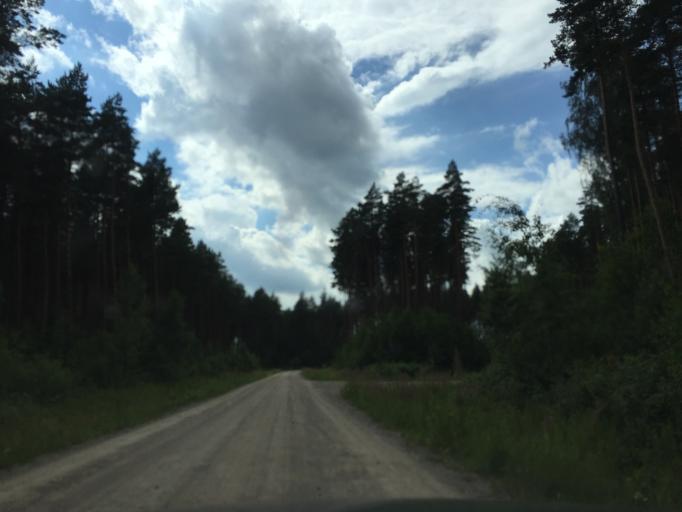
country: LV
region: Jelgava
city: Jelgava
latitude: 56.6262
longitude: 23.6302
